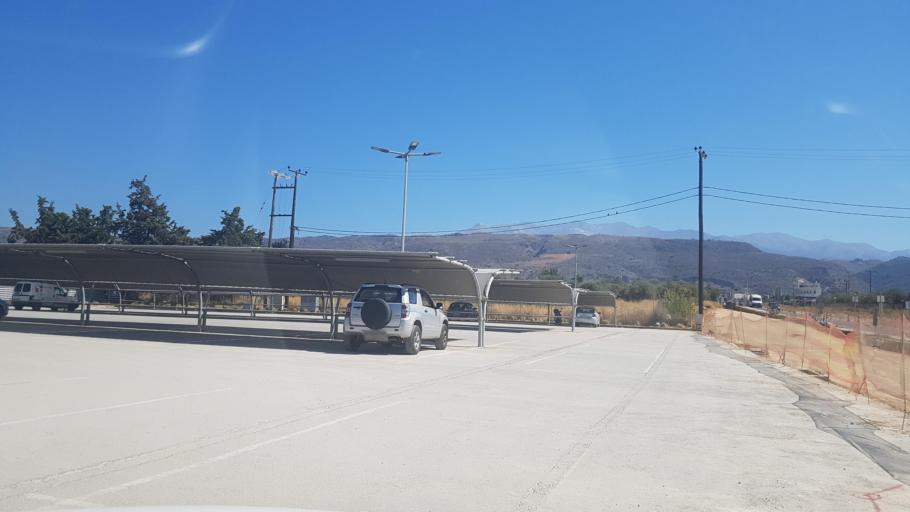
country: GR
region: Crete
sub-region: Nomos Chanias
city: Mournies
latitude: 35.4974
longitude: 24.0185
